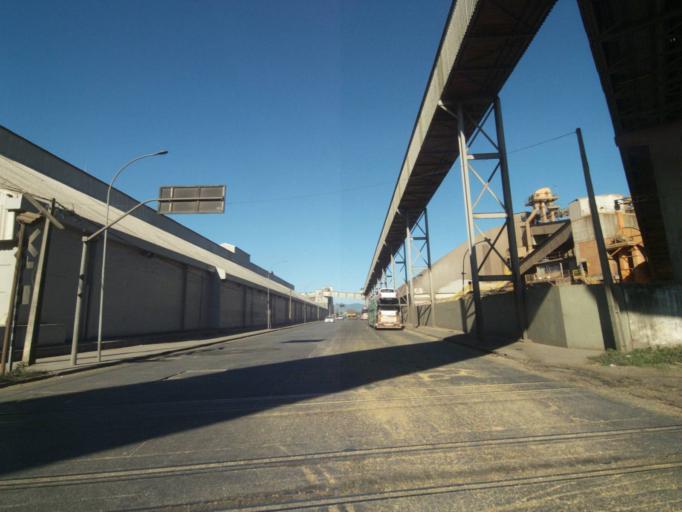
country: BR
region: Parana
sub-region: Paranagua
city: Paranagua
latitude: -25.5078
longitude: -48.5172
